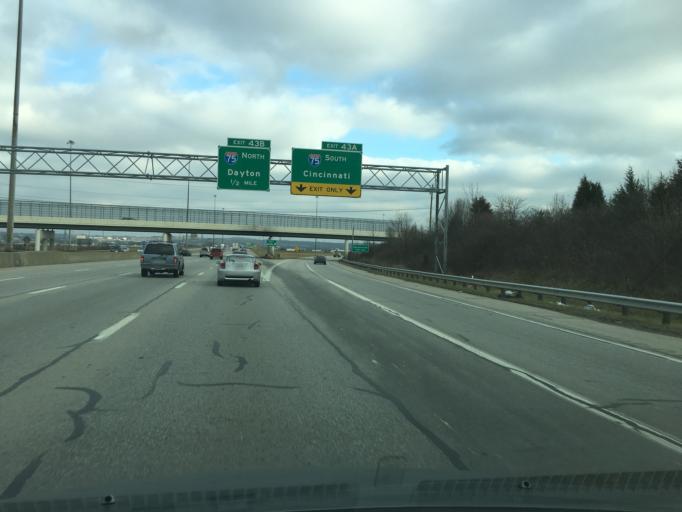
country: US
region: Ohio
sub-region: Hamilton County
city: Glendale
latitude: 39.2922
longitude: -84.4498
